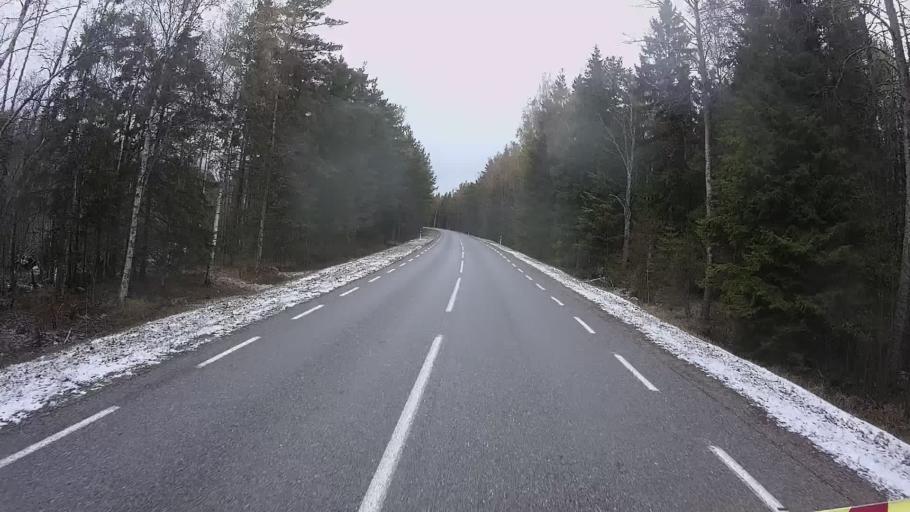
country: EE
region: Hiiumaa
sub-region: Kaerdla linn
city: Kardla
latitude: 59.0352
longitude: 22.6806
